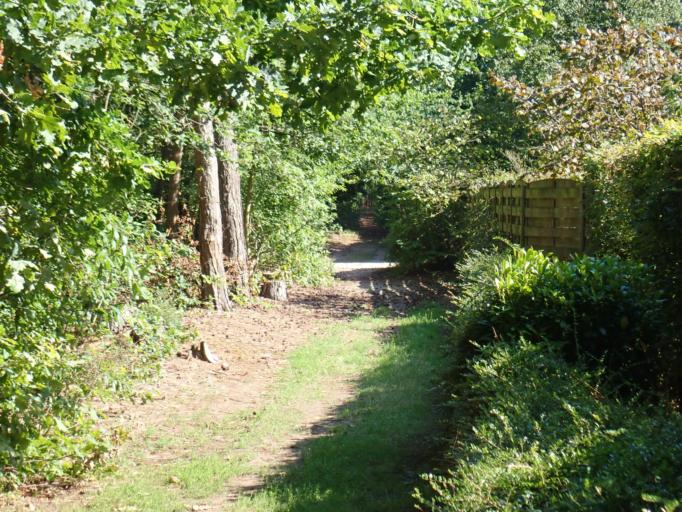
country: BE
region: Flanders
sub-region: Provincie Vlaams-Brabant
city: Scherpenheuvel-Zichem
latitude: 51.0511
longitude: 4.9758
